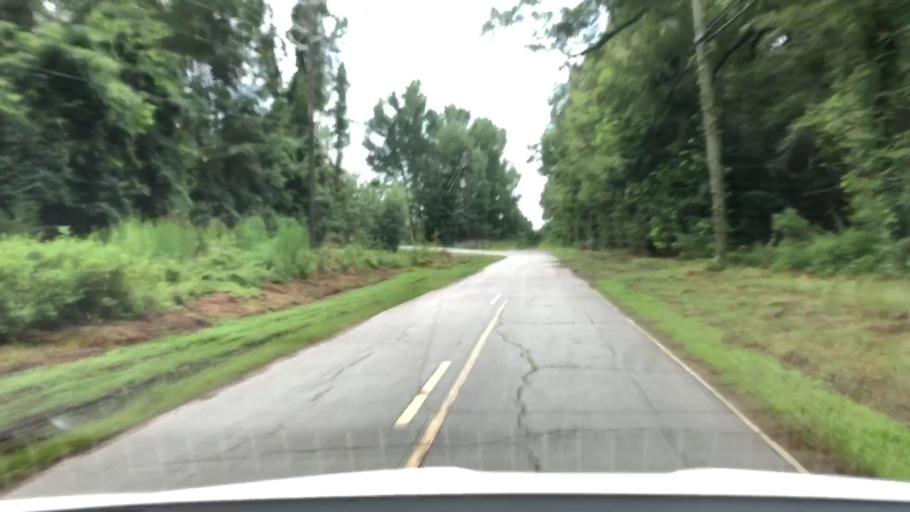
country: US
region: North Carolina
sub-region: Lenoir County
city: Kinston
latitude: 35.2574
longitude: -77.5977
